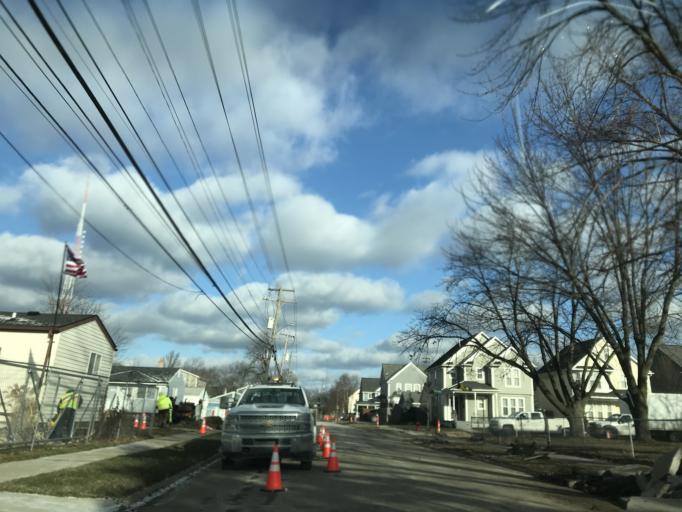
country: US
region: Michigan
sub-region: Oakland County
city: Hazel Park
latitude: 42.4665
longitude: -83.1133
